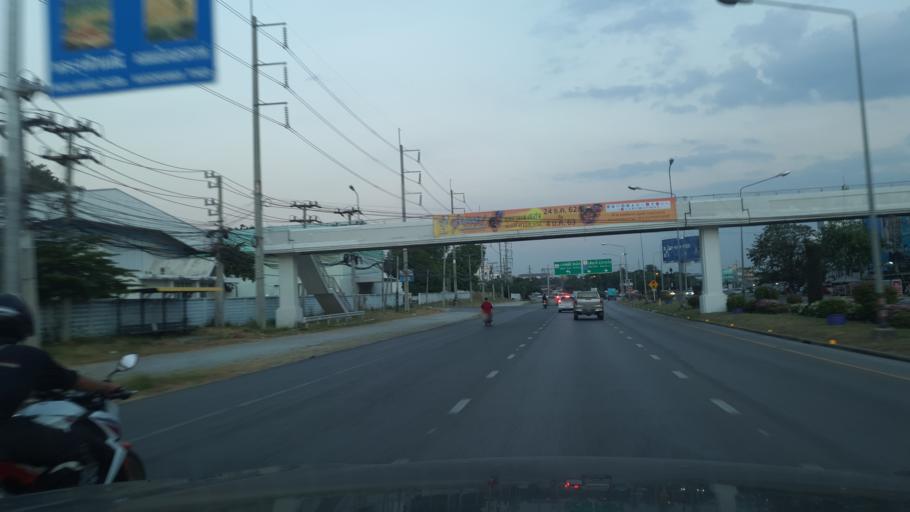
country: TH
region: Nakhon Sawan
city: Nakhon Sawan
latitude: 15.7069
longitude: 100.1080
